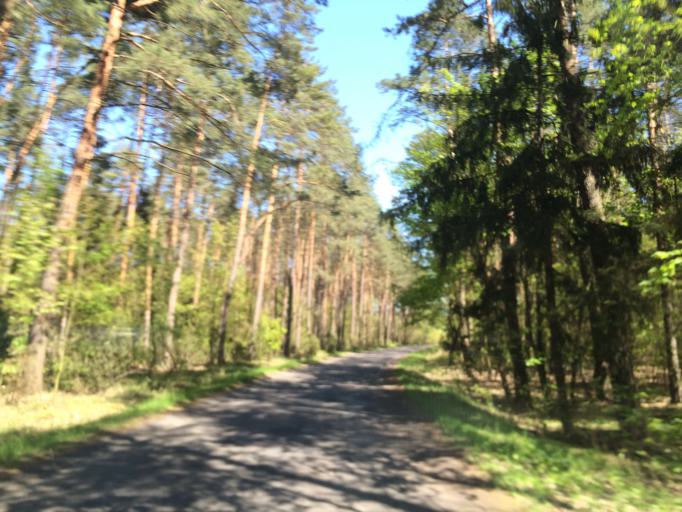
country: PL
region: Kujawsko-Pomorskie
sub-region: Powiat brodnicki
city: Brodnica
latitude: 53.3865
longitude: 19.4297
